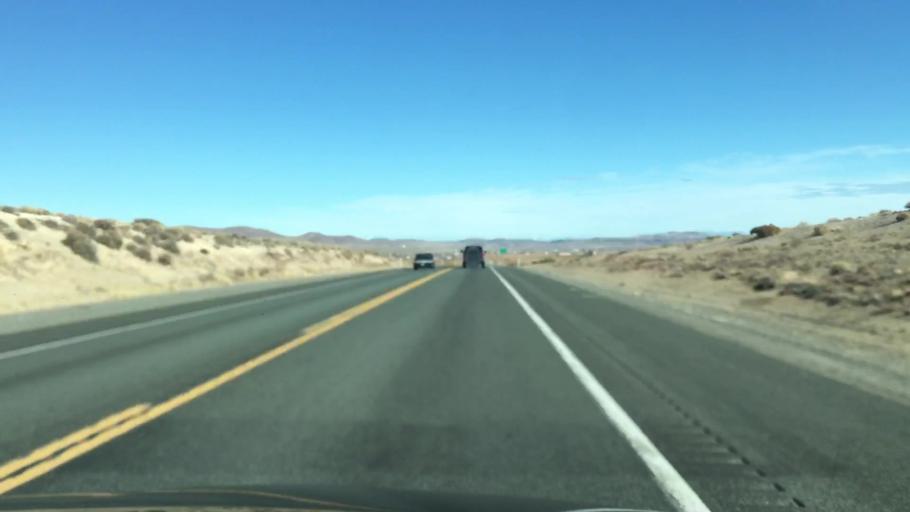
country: US
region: Nevada
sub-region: Lyon County
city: Stagecoach
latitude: 39.3812
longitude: -119.3204
